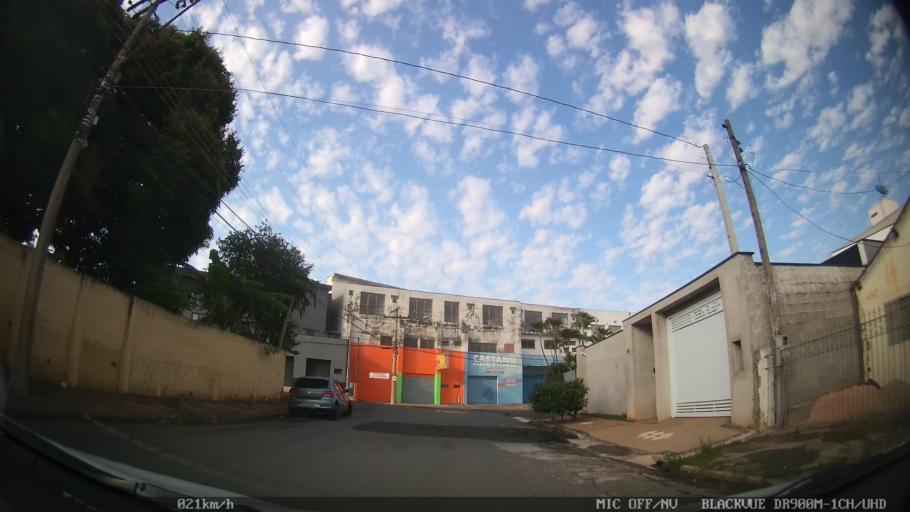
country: BR
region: Sao Paulo
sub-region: Americana
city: Americana
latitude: -22.7439
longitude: -47.3444
